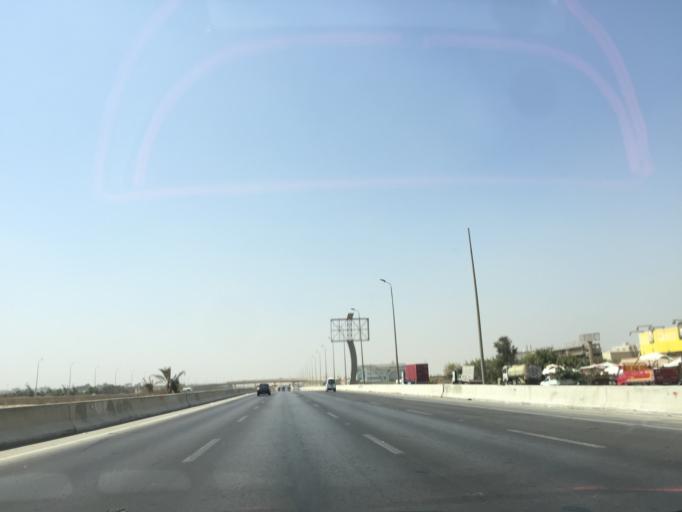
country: EG
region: Al Jizah
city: Awsim
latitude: 30.0761
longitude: 31.0040
